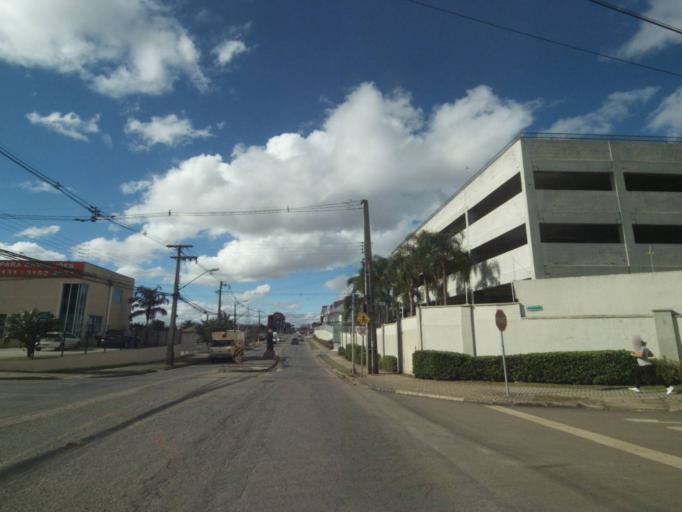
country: BR
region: Parana
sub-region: Sao Jose Dos Pinhais
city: Sao Jose dos Pinhais
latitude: -25.5301
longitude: -49.2947
